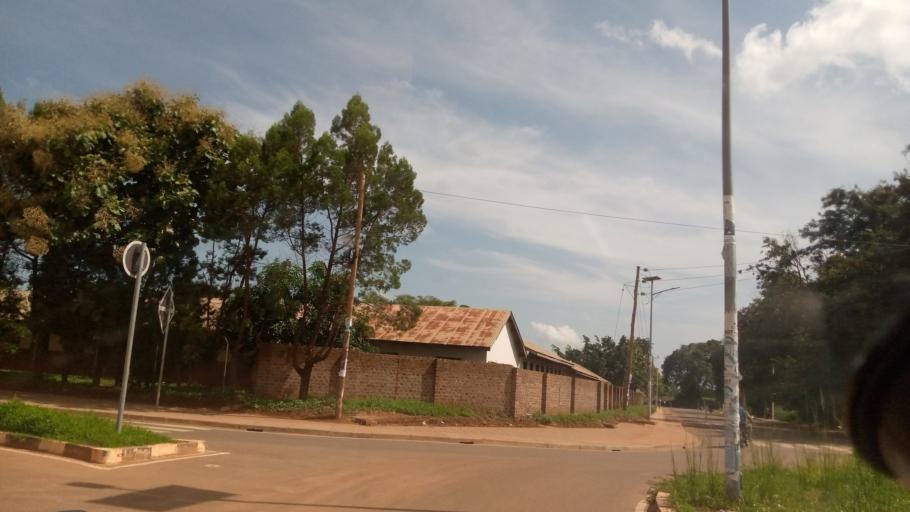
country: UG
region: Northern Region
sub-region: Gulu District
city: Gulu
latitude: 2.7707
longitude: 32.3082
